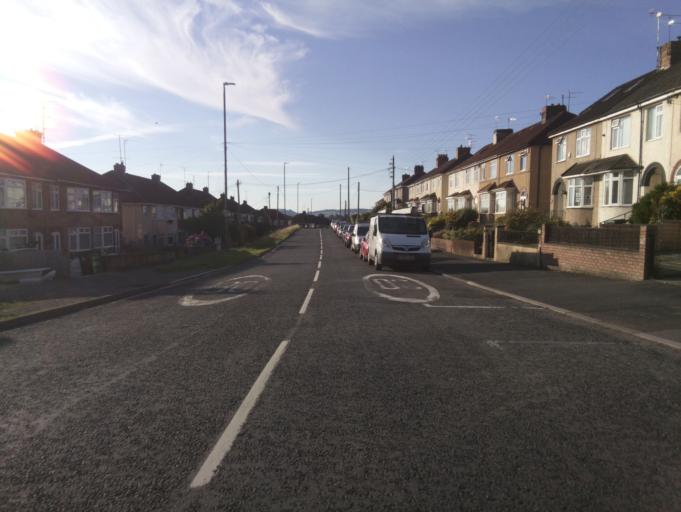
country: GB
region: England
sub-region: South Gloucestershire
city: Mangotsfield
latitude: 51.4767
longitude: -2.4952
